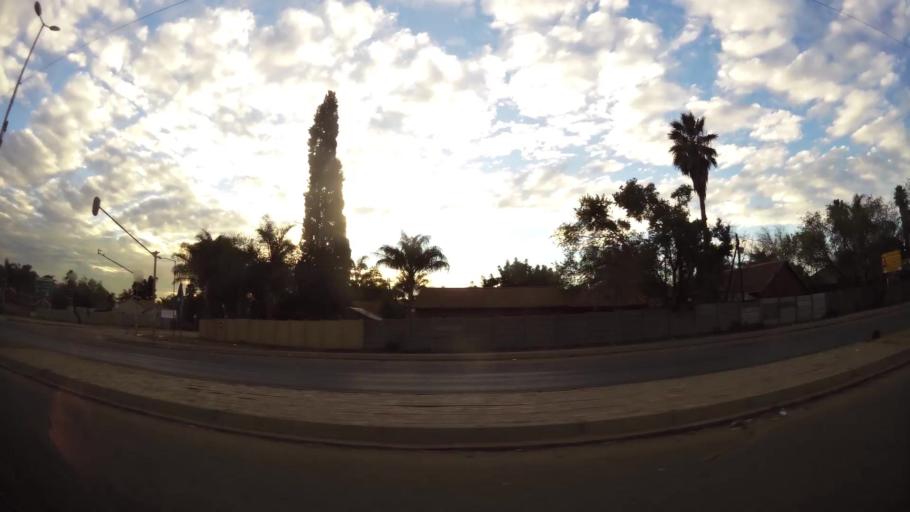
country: ZA
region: Gauteng
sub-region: City of Tshwane Metropolitan Municipality
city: Pretoria
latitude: -25.7325
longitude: 28.3164
